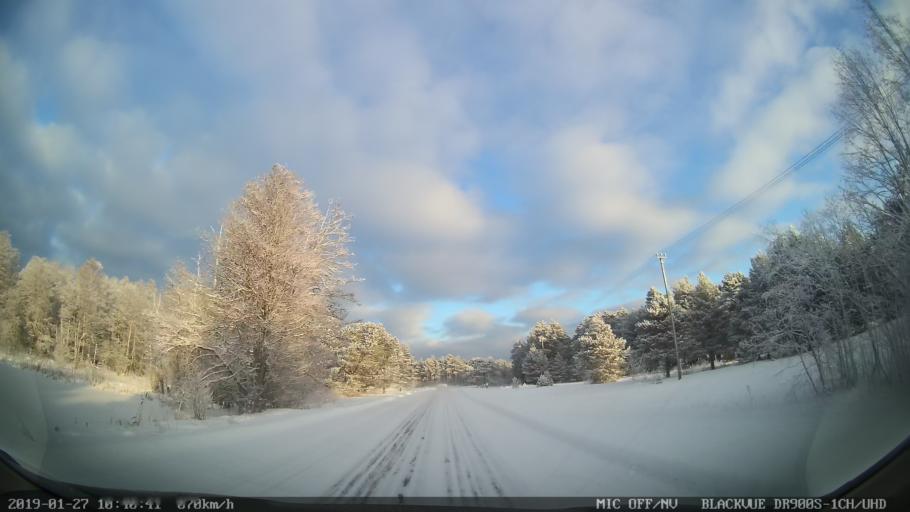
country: EE
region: Harju
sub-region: Raasiku vald
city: Raasiku
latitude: 59.5052
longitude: 25.2624
